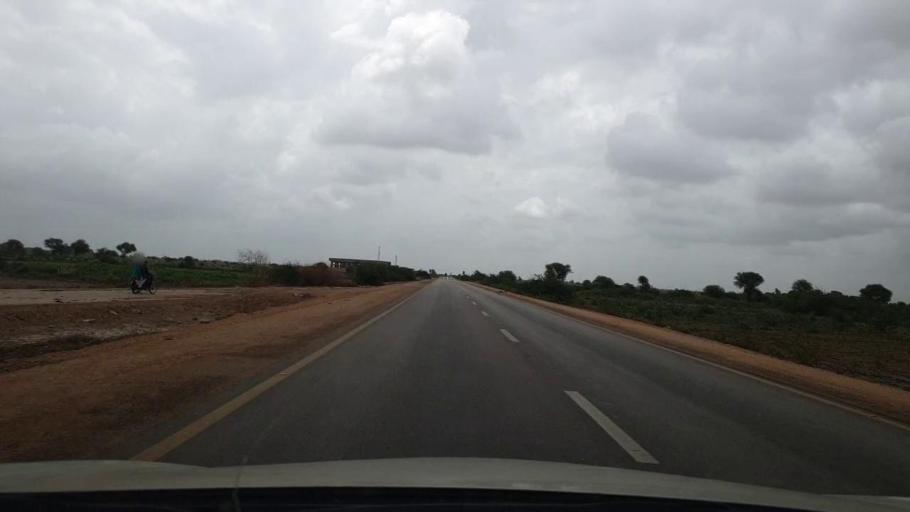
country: PK
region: Sindh
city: Mirpur Batoro
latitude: 24.6384
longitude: 68.3880
